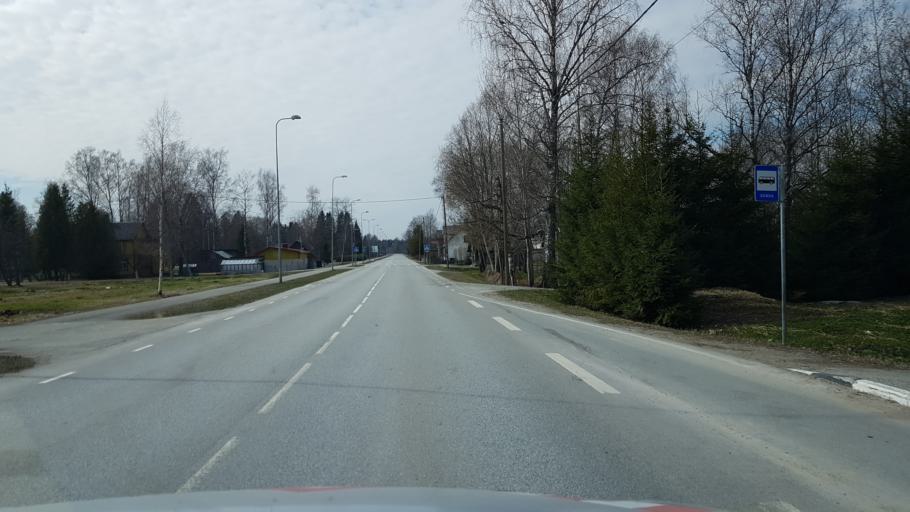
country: EE
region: Ida-Virumaa
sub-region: Aseri vald
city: Aseri
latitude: 59.3519
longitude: 26.8419
